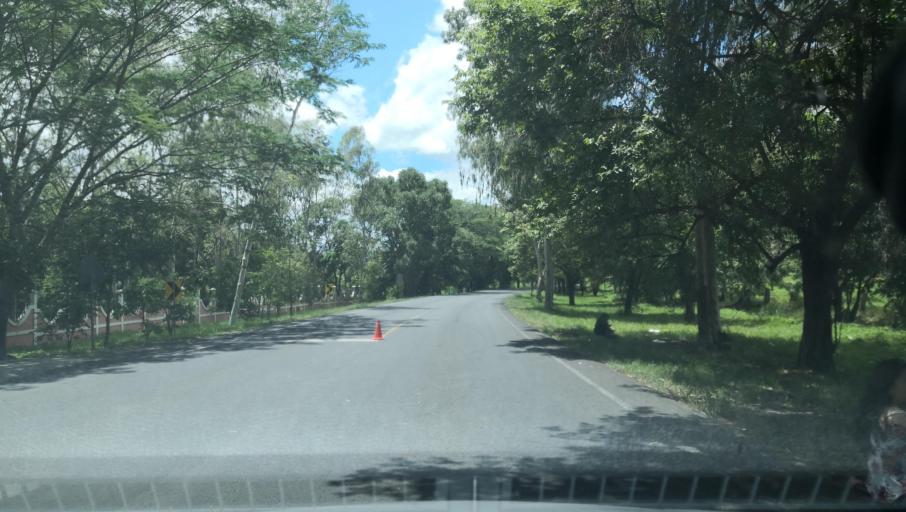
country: NI
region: Esteli
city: Condega
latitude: 13.2463
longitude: -86.3720
